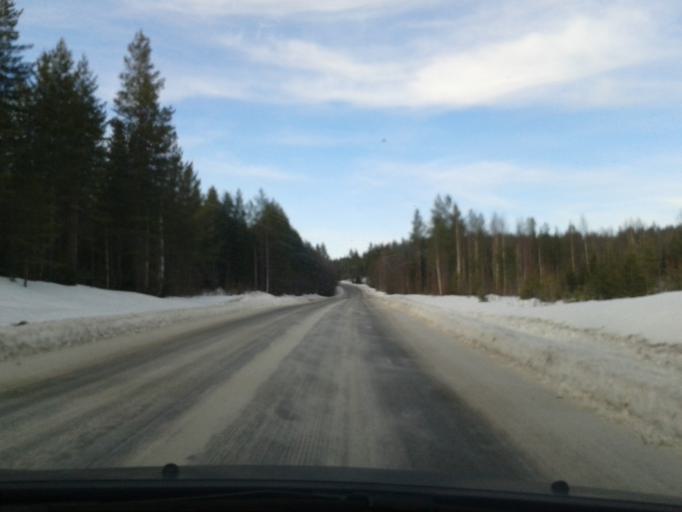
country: SE
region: Vaesternorrland
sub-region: OErnskoeldsviks Kommun
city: Bredbyn
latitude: 63.5790
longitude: 17.9216
